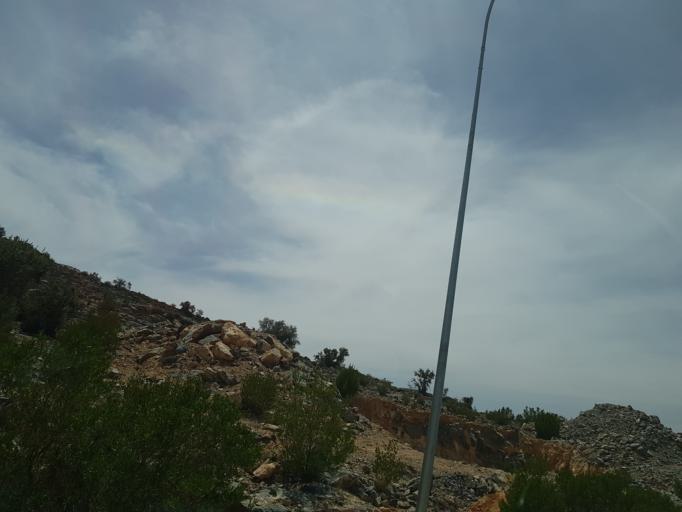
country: OM
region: Al Batinah
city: Bayt al `Awabi
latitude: 23.1388
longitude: 57.5418
